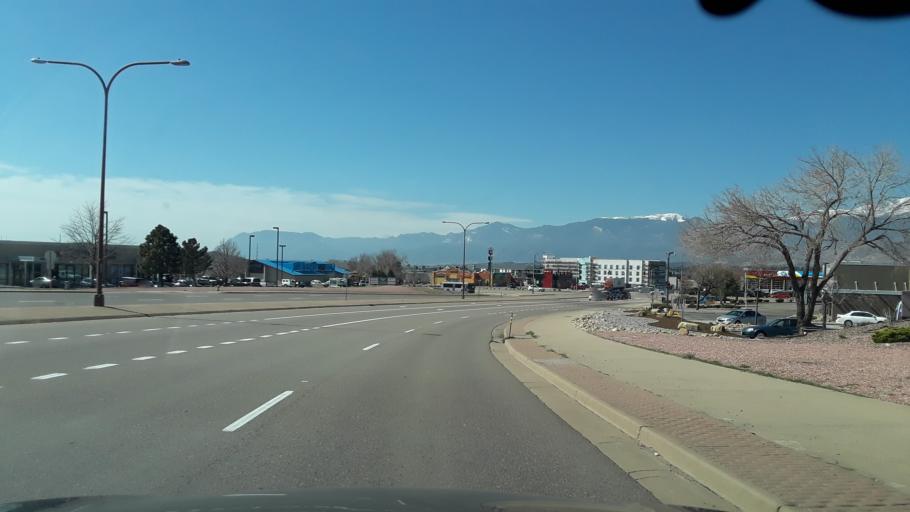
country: US
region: Colorado
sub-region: El Paso County
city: Air Force Academy
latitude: 38.9500
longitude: -104.8021
